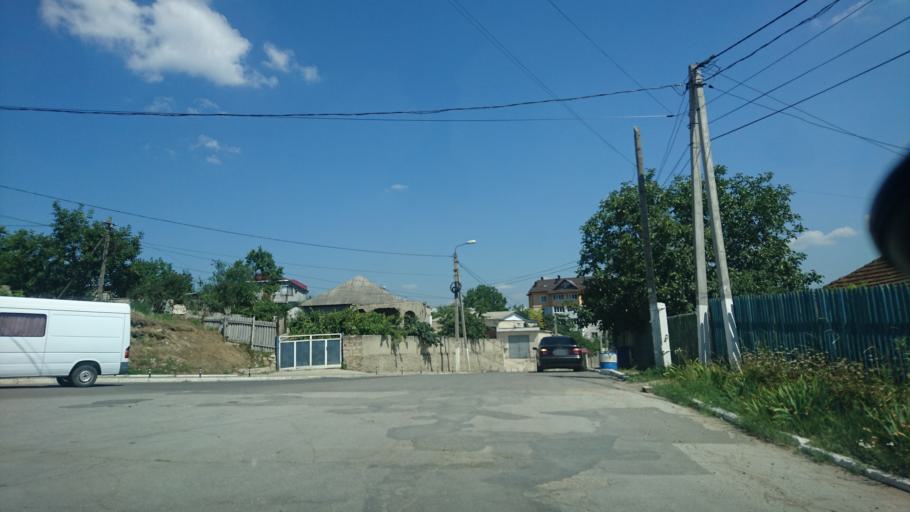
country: MD
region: Chisinau
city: Vatra
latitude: 47.0190
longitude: 28.7664
